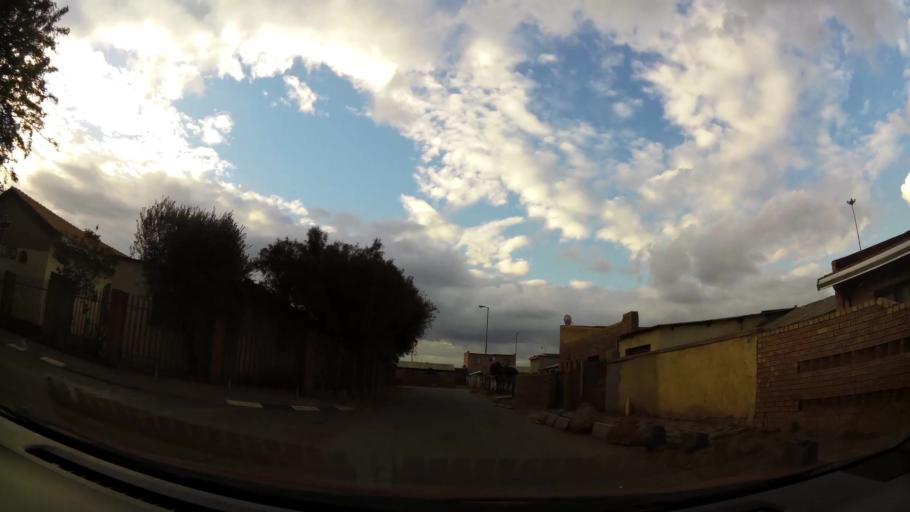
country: ZA
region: Gauteng
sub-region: City of Johannesburg Metropolitan Municipality
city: Soweto
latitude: -26.2454
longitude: 27.8278
